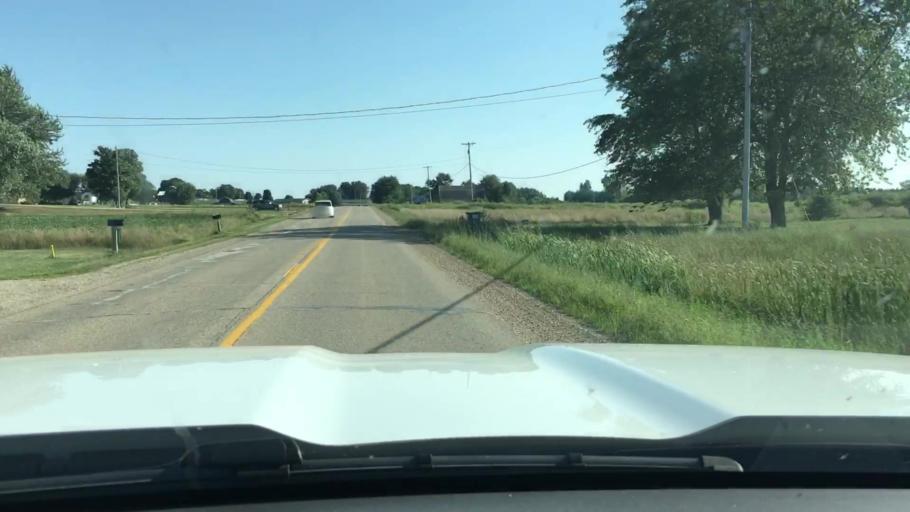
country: US
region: Michigan
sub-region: Ottawa County
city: Zeeland
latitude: 42.8613
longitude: -85.9600
